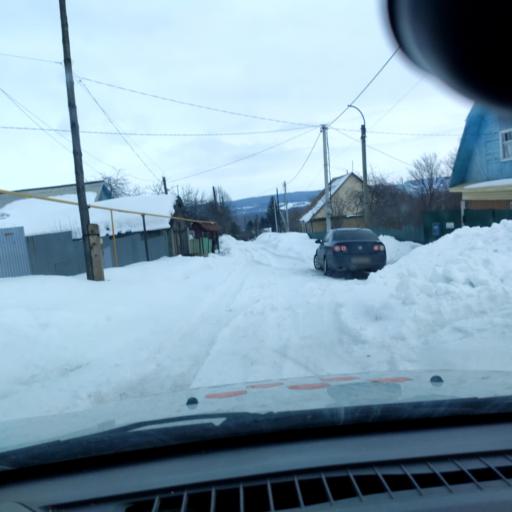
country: RU
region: Bashkortostan
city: Avdon
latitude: 54.6212
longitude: 55.6476
